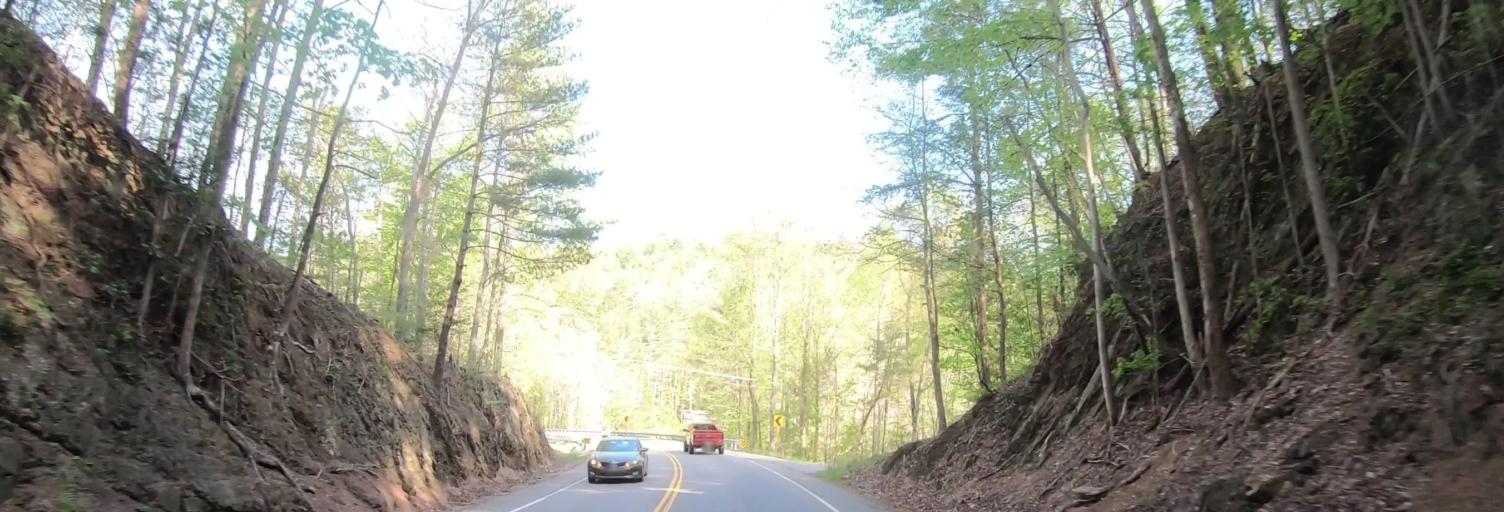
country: US
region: Tennessee
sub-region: Blount County
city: Wildwood
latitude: 35.6989
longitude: -83.8084
